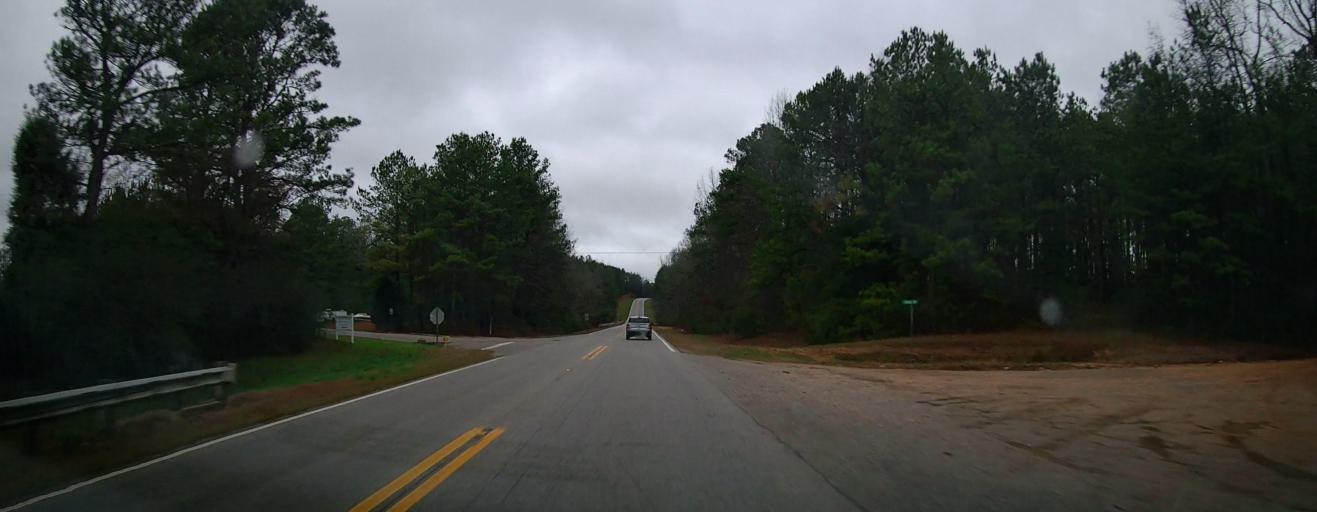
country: US
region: Alabama
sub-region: Bibb County
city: Centreville
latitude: 32.8685
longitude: -86.9731
